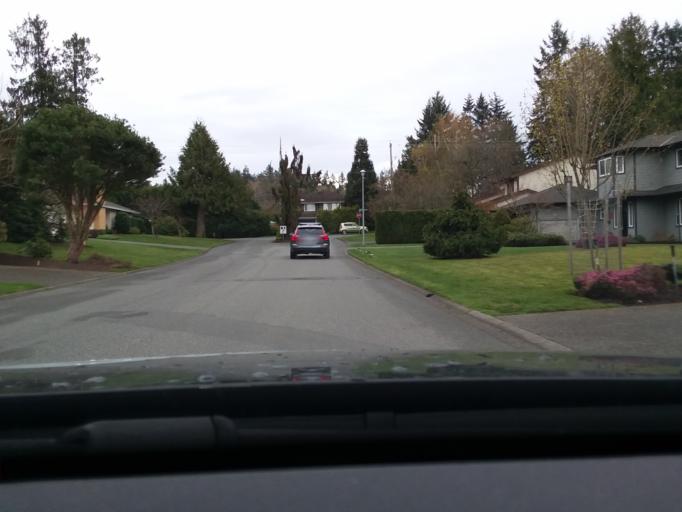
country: CA
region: British Columbia
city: Victoria
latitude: 48.5150
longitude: -123.3785
